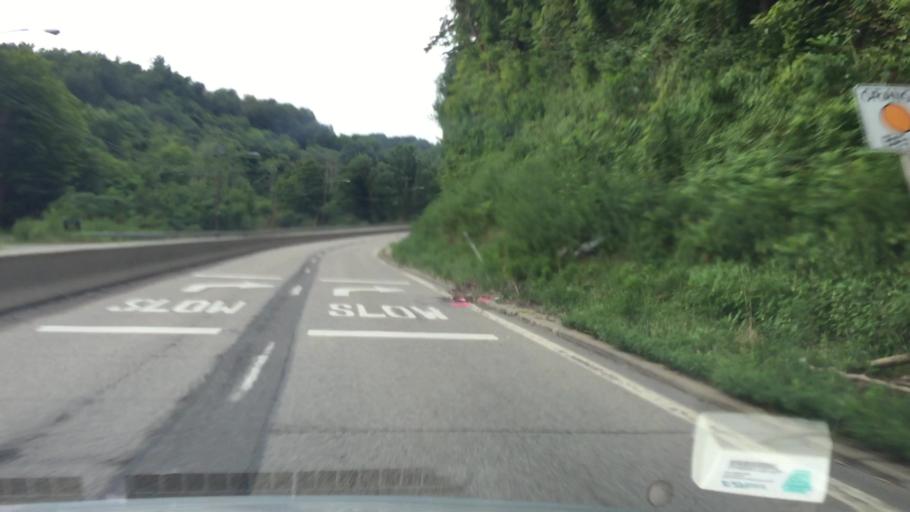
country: US
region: Pennsylvania
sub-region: Allegheny County
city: Carnot-Moon
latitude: 40.5305
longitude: -80.2050
